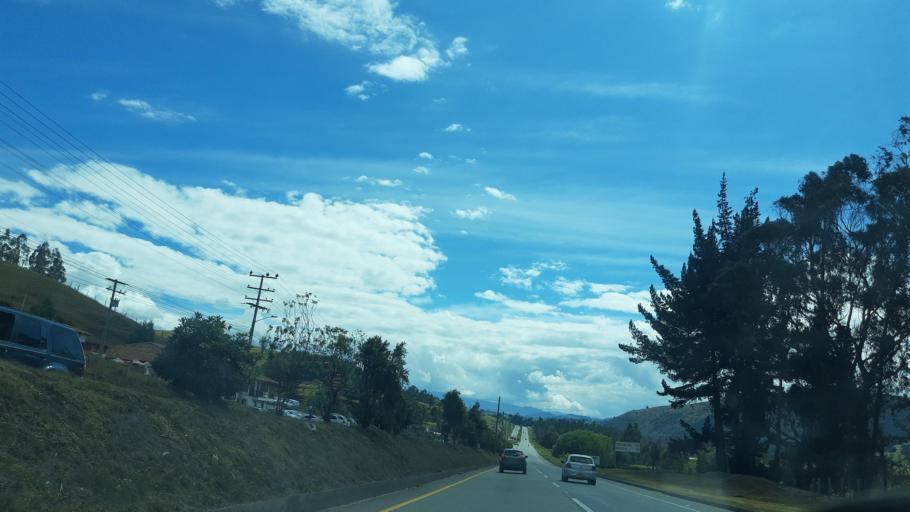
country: CO
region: Cundinamarca
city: Choconta
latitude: 5.1412
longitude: -73.6909
